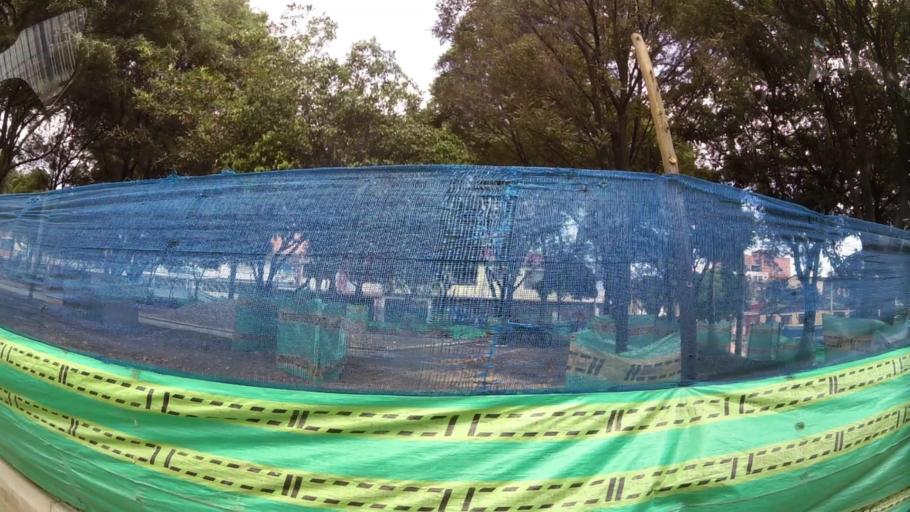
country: CO
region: Bogota D.C.
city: Bogota
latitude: 4.5808
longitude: -74.0988
